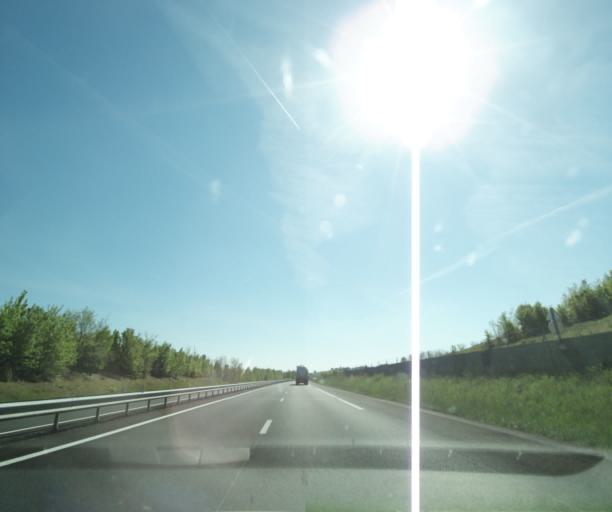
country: FR
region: Midi-Pyrenees
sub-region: Departement du Tarn-et-Garonne
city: Caussade
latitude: 44.1708
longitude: 1.5276
